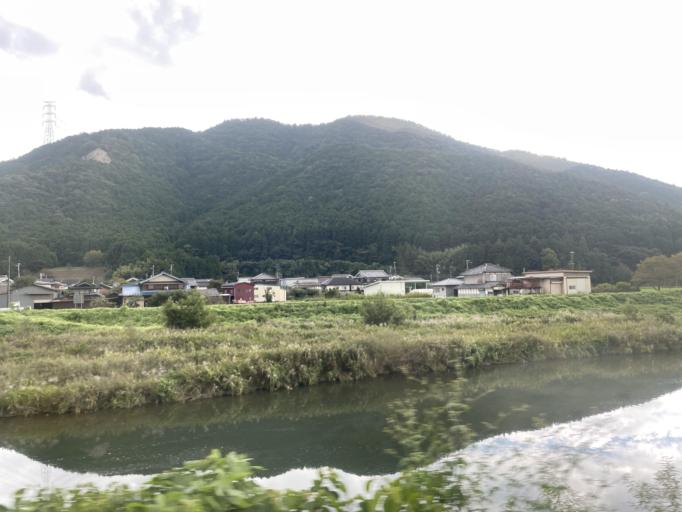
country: JP
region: Hyogo
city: Nishiwaki
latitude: 35.0819
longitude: 135.0536
